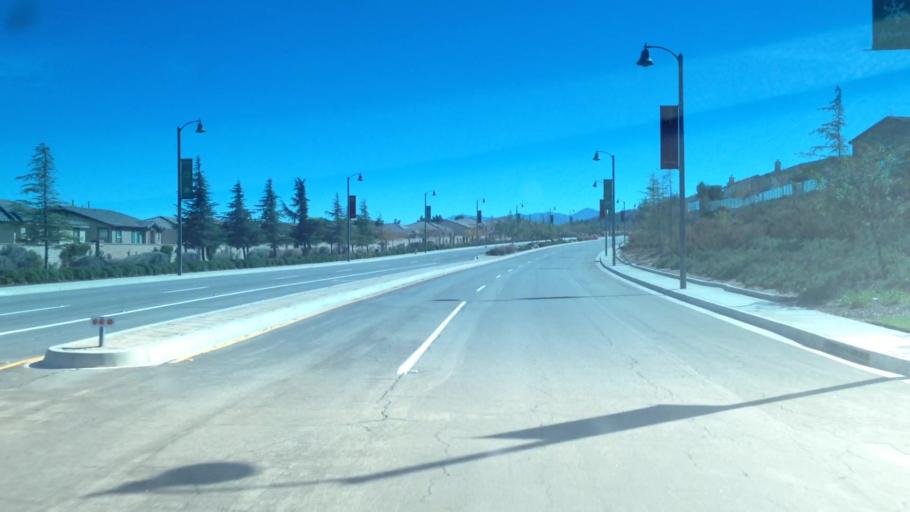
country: US
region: California
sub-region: Los Angeles County
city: Desert View Highlands
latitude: 34.5641
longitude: -118.1722
